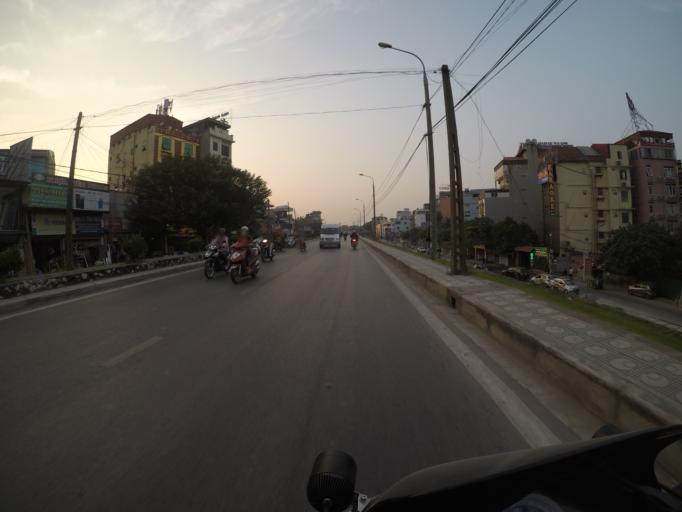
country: VN
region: Ha Noi
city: Hoan Kiem
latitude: 21.0380
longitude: 105.8686
